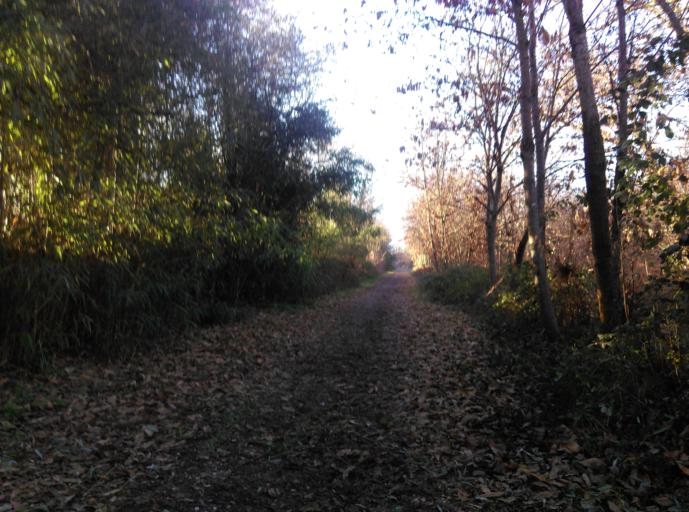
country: FR
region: Aquitaine
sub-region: Departement de la Gironde
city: Villenave-d'Ornon
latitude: 44.7734
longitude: -0.5525
